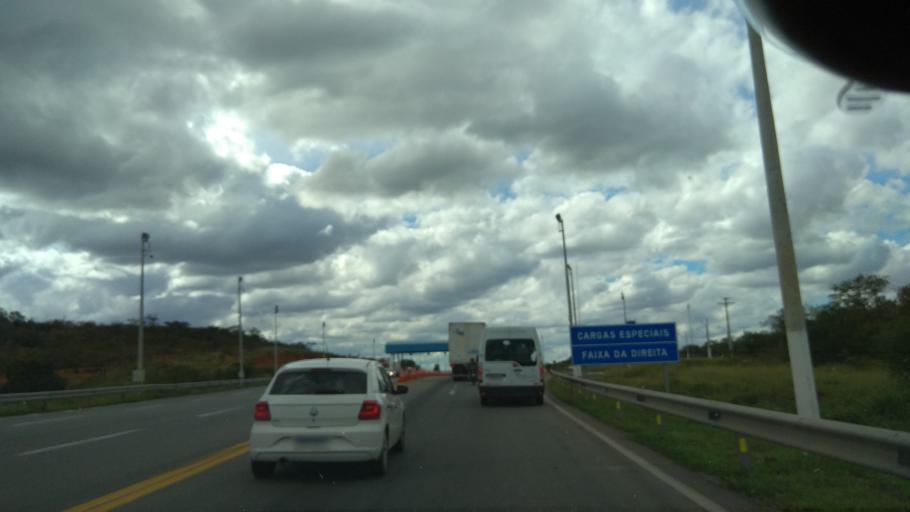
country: BR
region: Bahia
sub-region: Santa Ines
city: Santa Ines
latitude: -13.0105
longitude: -39.9574
